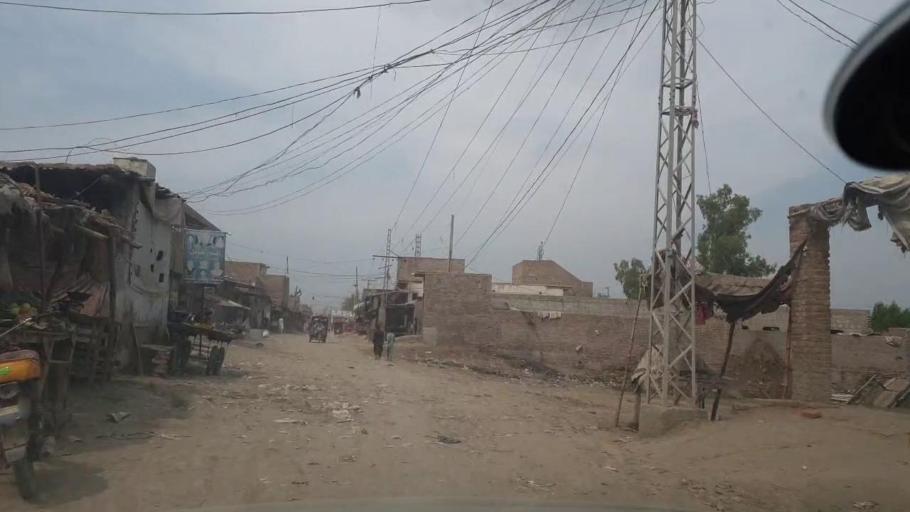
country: PK
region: Sindh
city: Jacobabad
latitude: 28.2670
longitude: 68.4377
